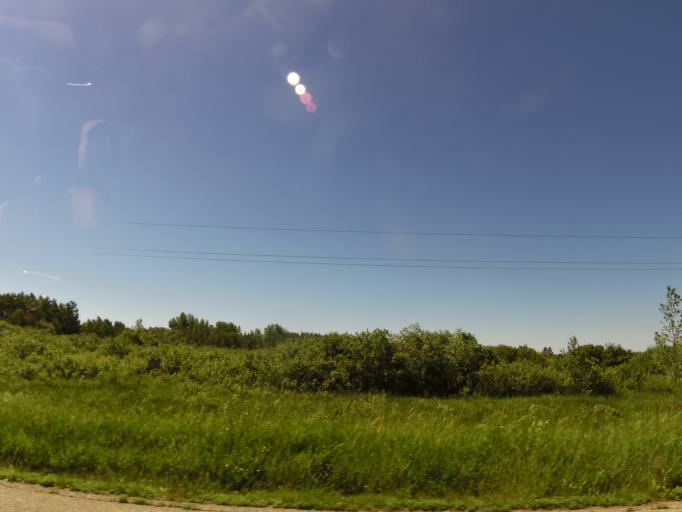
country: US
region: Minnesota
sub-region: Red Lake County
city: Red Lake Falls
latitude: 47.7604
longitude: -96.4140
